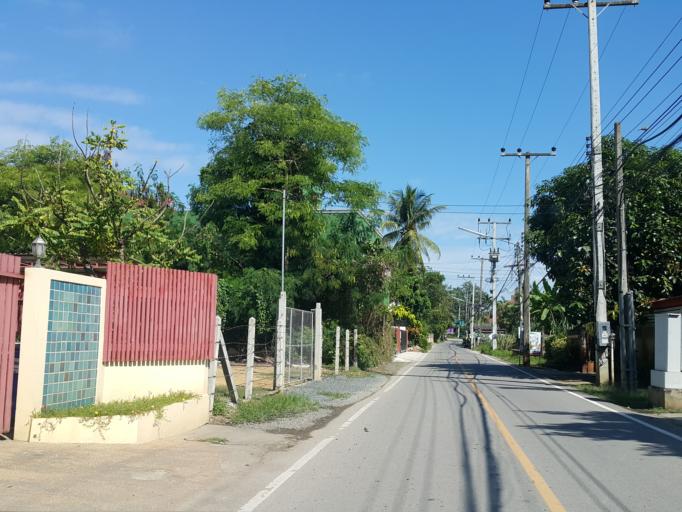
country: TH
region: Chiang Mai
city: San Sai
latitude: 18.8129
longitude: 99.0340
